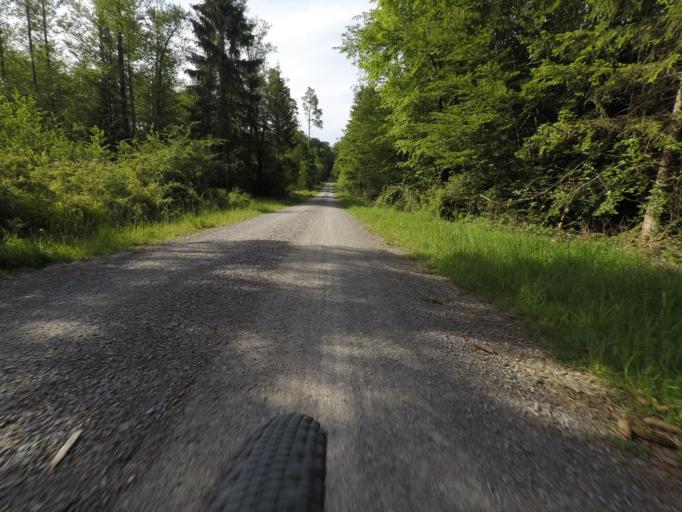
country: DE
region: Baden-Wuerttemberg
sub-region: Regierungsbezirk Stuttgart
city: Weil im Schonbuch
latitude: 48.5944
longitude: 9.0560
